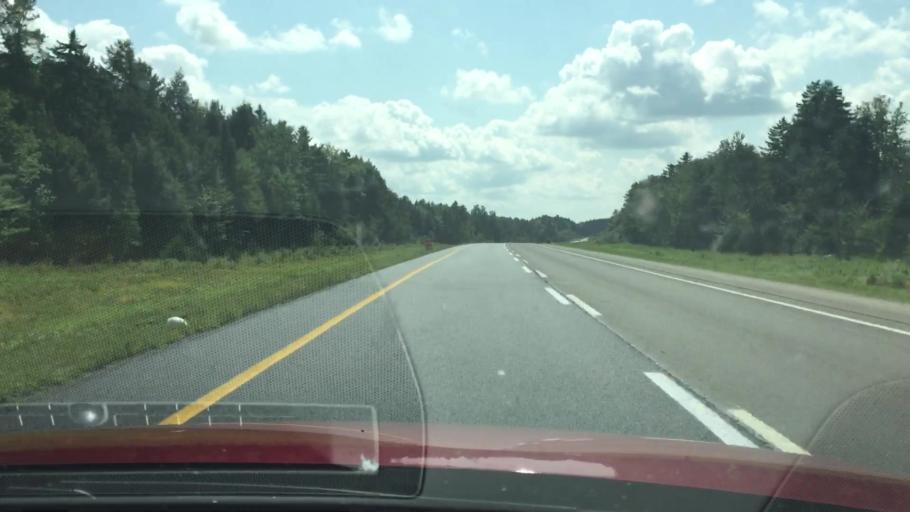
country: US
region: Maine
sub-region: Penobscot County
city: Medway
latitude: 45.6916
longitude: -68.4883
